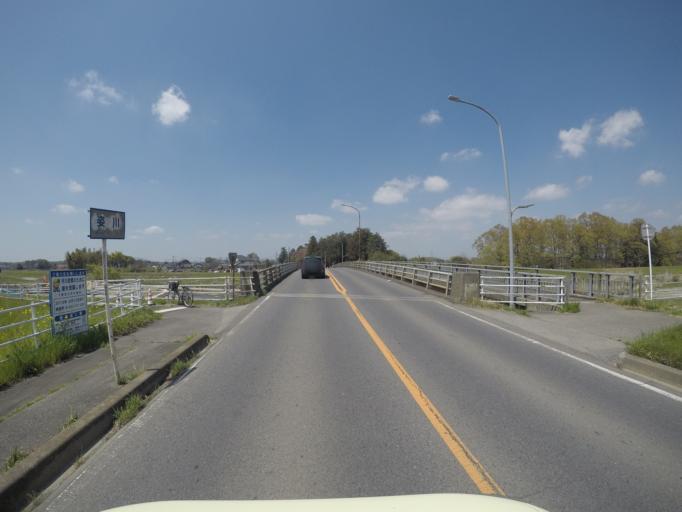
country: JP
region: Tochigi
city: Mibu
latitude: 36.3895
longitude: 139.8288
